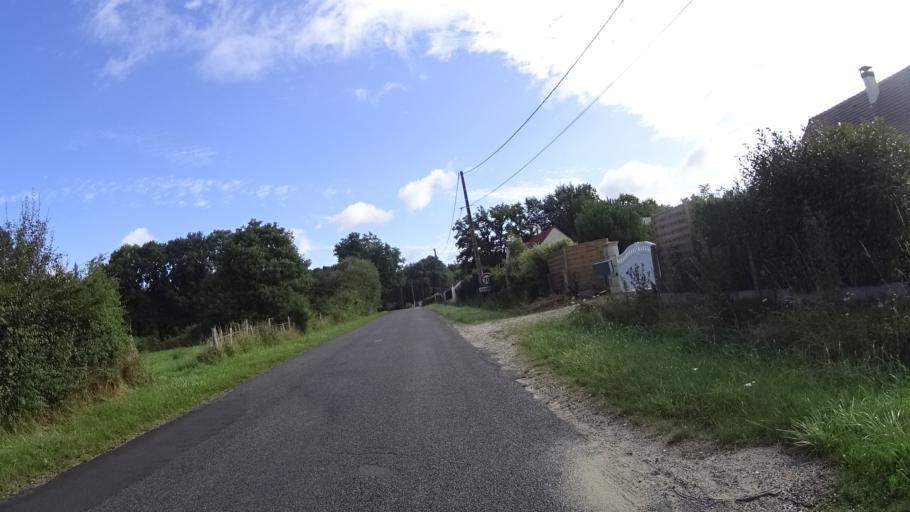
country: FR
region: Centre
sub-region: Departement du Loiret
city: Bouzy-la-Foret
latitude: 47.8773
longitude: 2.4411
